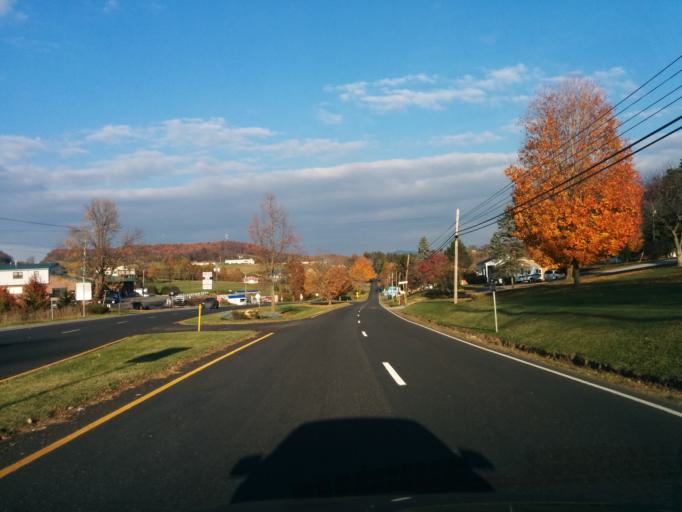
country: US
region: Virginia
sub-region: City of Buena Vista
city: Buena Vista
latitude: 37.8814
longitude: -79.2851
